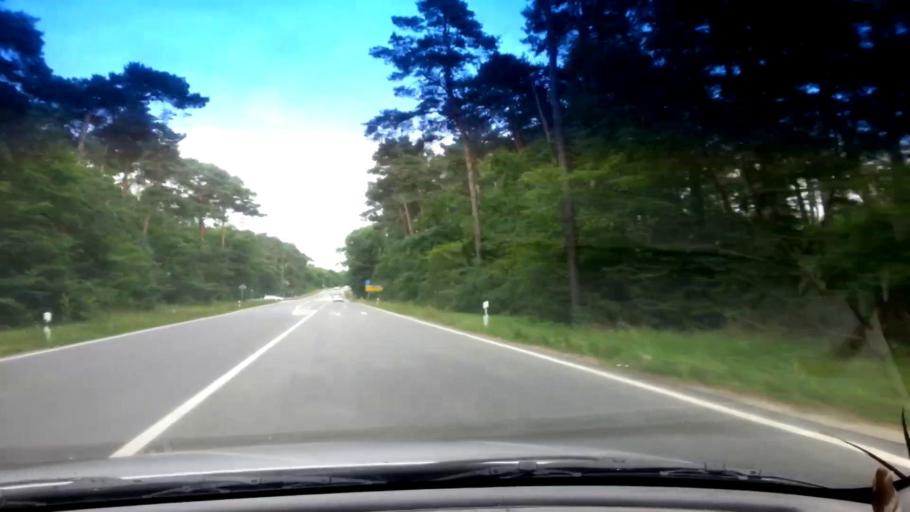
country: DE
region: Bavaria
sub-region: Upper Franconia
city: Strullendorf
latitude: 49.8309
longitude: 10.9793
